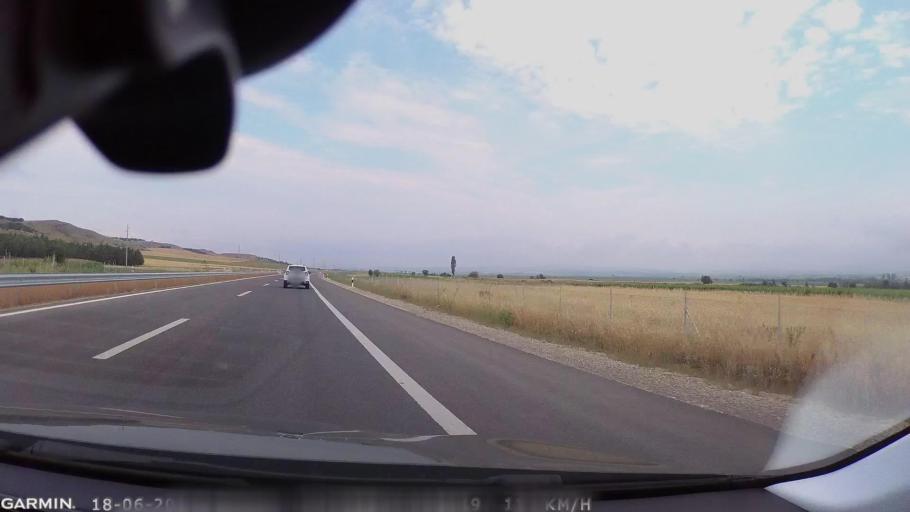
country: MK
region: Stip
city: Shtip
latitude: 41.7980
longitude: 22.0839
